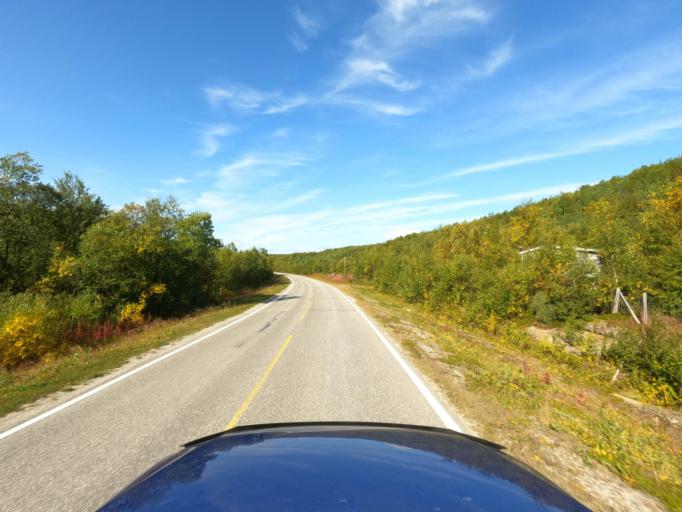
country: NO
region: Finnmark Fylke
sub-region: Porsanger
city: Lakselv
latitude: 69.7611
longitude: 25.2035
